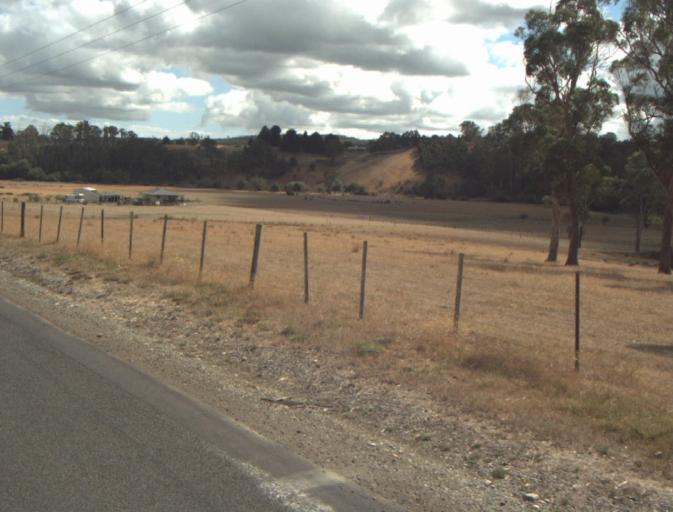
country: AU
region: Tasmania
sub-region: Launceston
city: Mayfield
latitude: -41.2290
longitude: 147.1444
